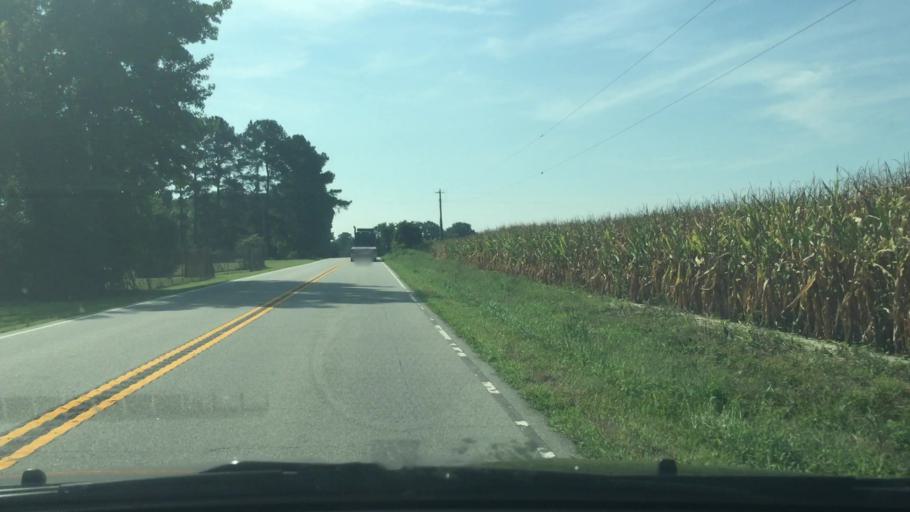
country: US
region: Virginia
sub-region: Sussex County
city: Sussex
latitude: 36.8829
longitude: -77.1533
